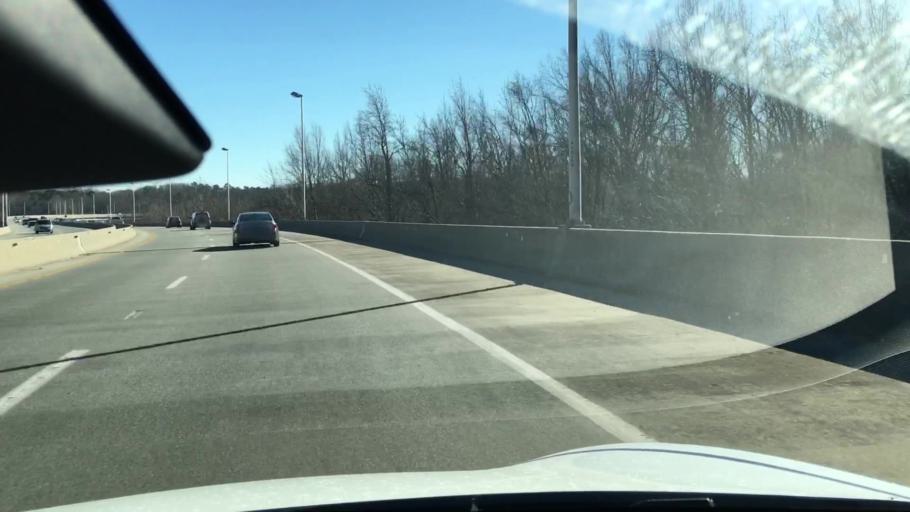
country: US
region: Virginia
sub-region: Henrico County
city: Tuckahoe
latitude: 37.5633
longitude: -77.5765
